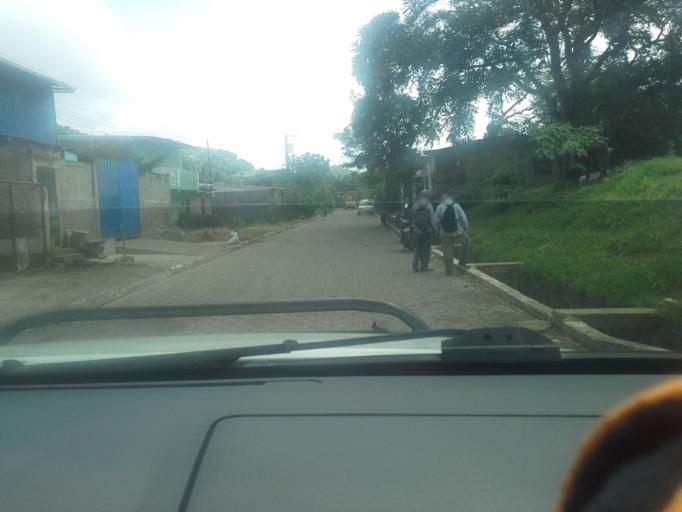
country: NI
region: Matagalpa
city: Matagalpa
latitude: 12.9217
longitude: -85.9259
